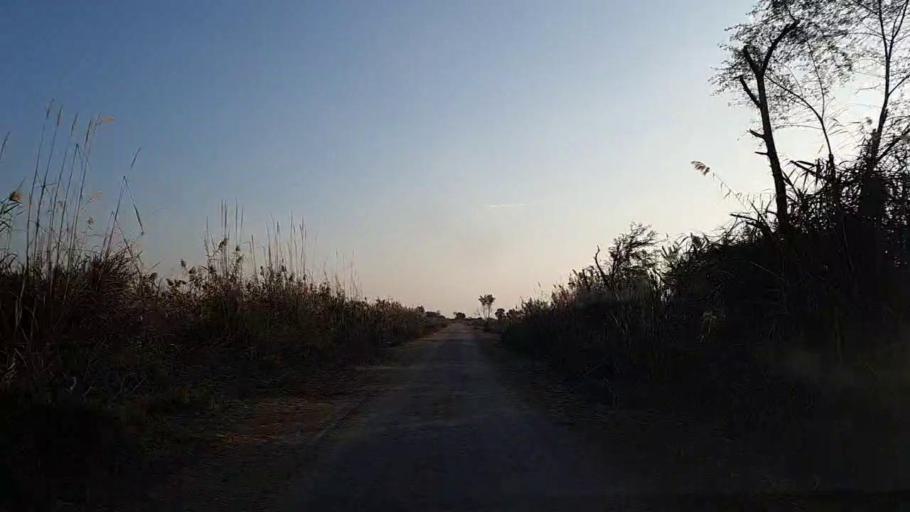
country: PK
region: Sindh
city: Sanghar
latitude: 26.2691
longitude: 68.9820
